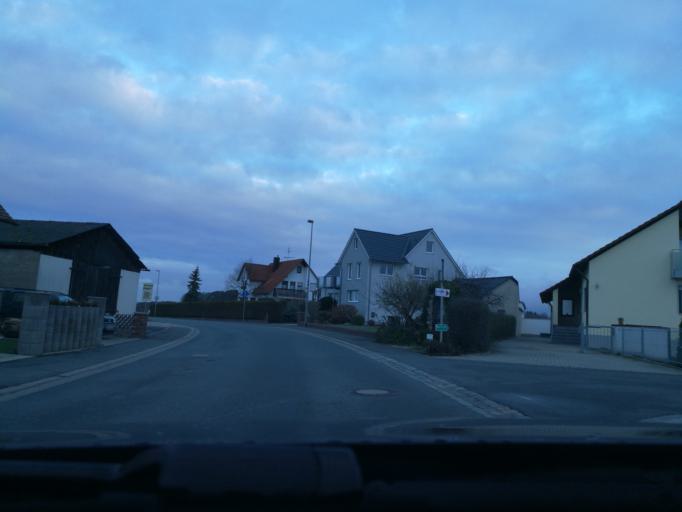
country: DE
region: Bavaria
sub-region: Upper Franconia
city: Langensendelbach
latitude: 49.6448
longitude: 11.0692
